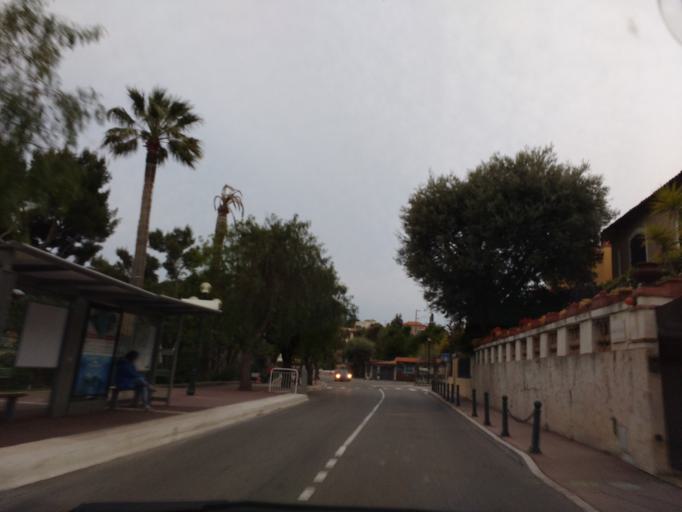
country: FR
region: Provence-Alpes-Cote d'Azur
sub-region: Departement des Alpes-Maritimes
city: Beaulieu-sur-Mer
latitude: 43.7034
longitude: 7.3302
